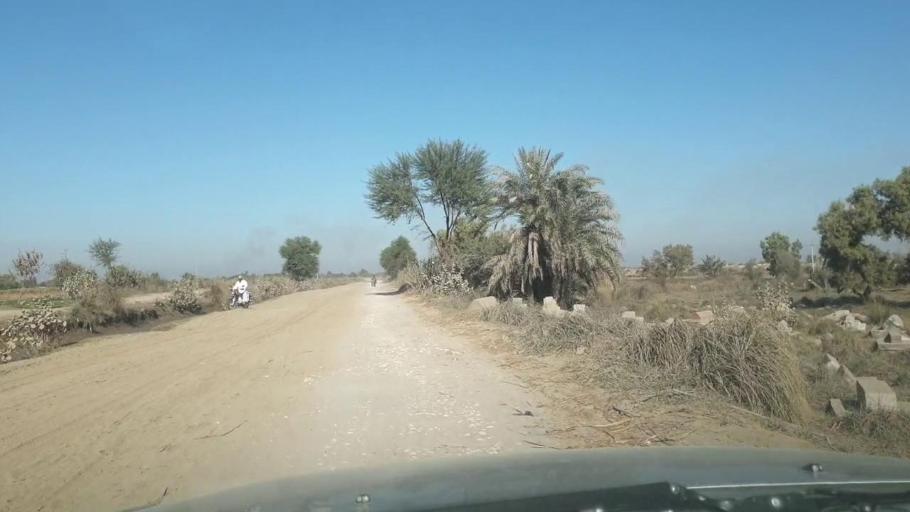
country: PK
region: Sindh
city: Ghotki
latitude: 28.0776
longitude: 69.3462
